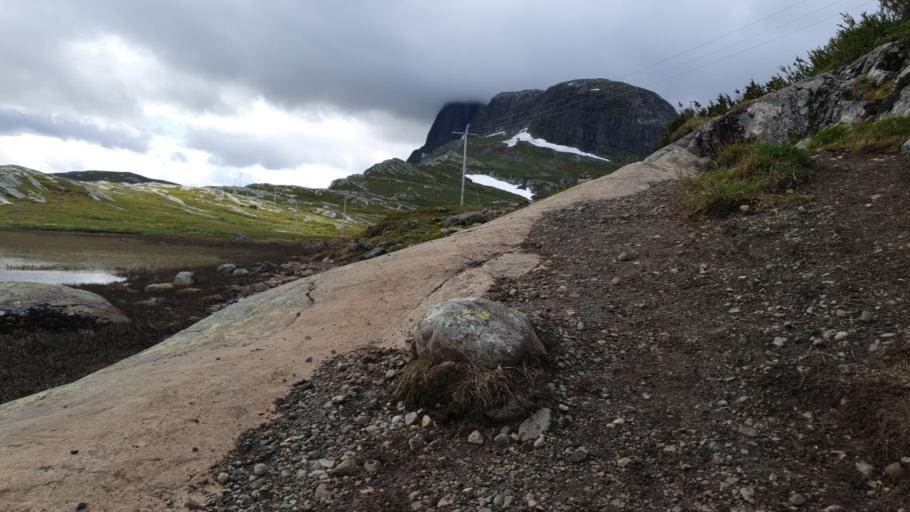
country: NO
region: Oppland
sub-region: Vestre Slidre
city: Slidre
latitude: 61.3176
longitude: 8.8039
